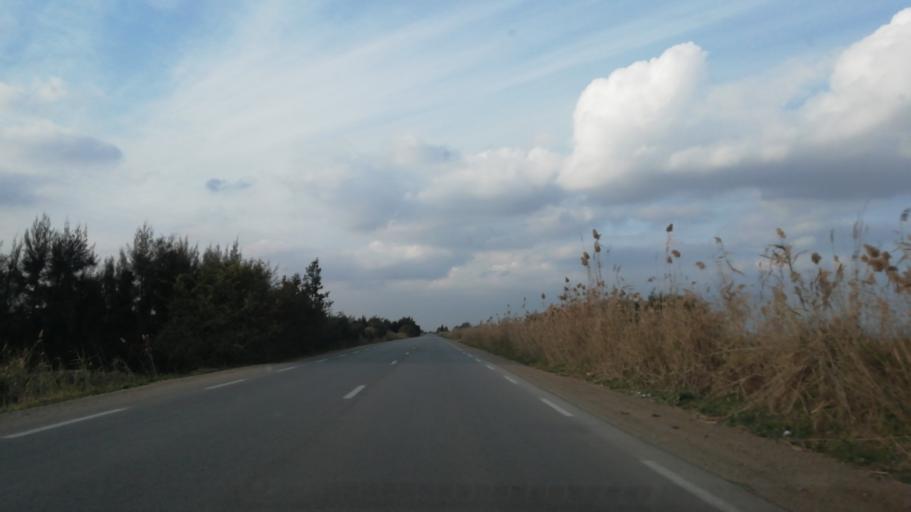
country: DZ
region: Mascara
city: Sig
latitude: 35.6421
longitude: 0.0304
